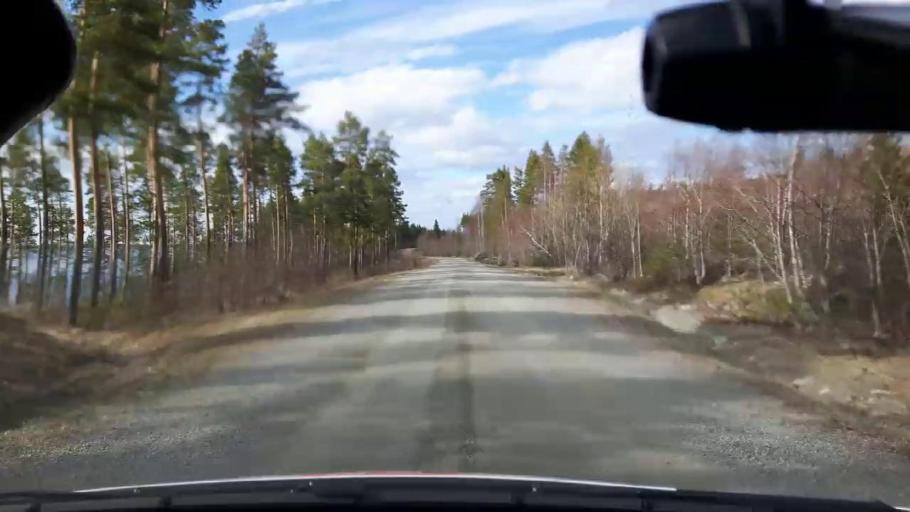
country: SE
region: Jaemtland
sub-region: Bergs Kommun
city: Hoverberg
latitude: 62.7320
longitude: 14.6650
